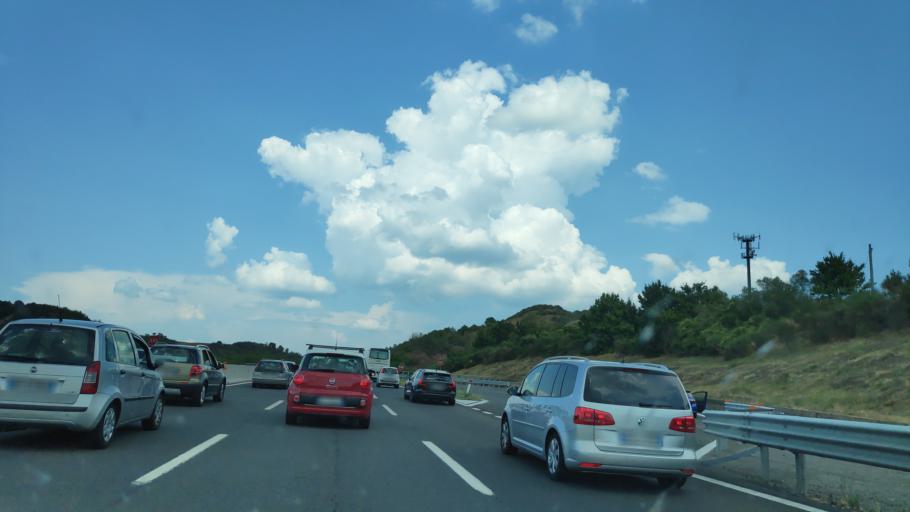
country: IT
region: Umbria
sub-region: Provincia di Terni
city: Ficulle
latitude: 42.8299
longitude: 12.0427
